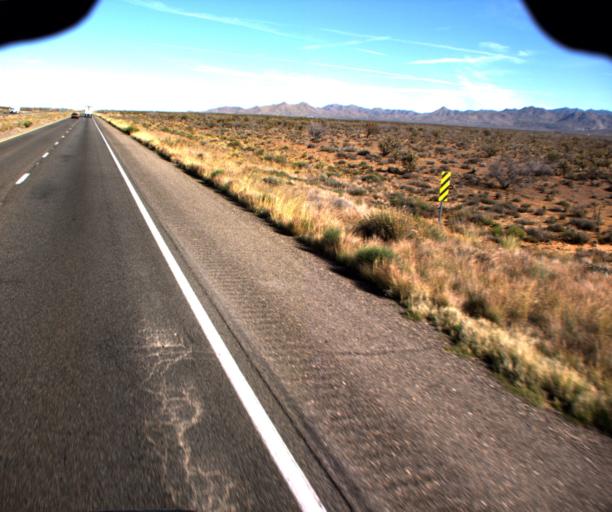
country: US
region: Arizona
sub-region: Mohave County
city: Golden Valley
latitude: 35.3478
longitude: -114.2236
